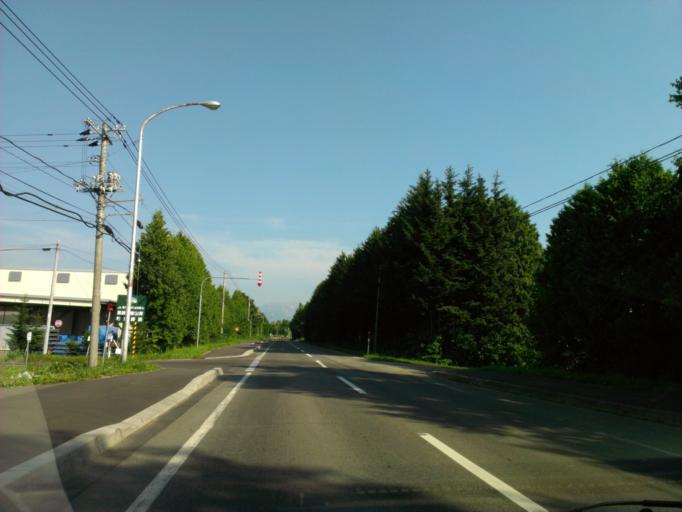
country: JP
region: Hokkaido
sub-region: Asahikawa-shi
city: Asahikawa
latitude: 43.5801
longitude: 142.4857
